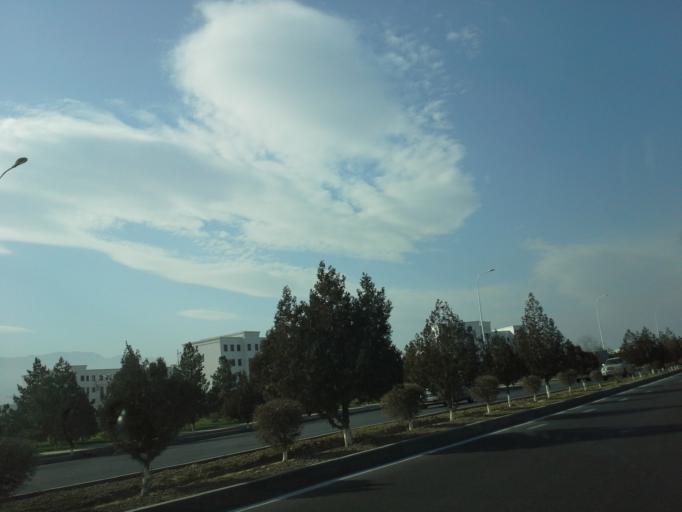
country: TM
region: Ahal
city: Abadan
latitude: 38.0427
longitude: 58.2072
